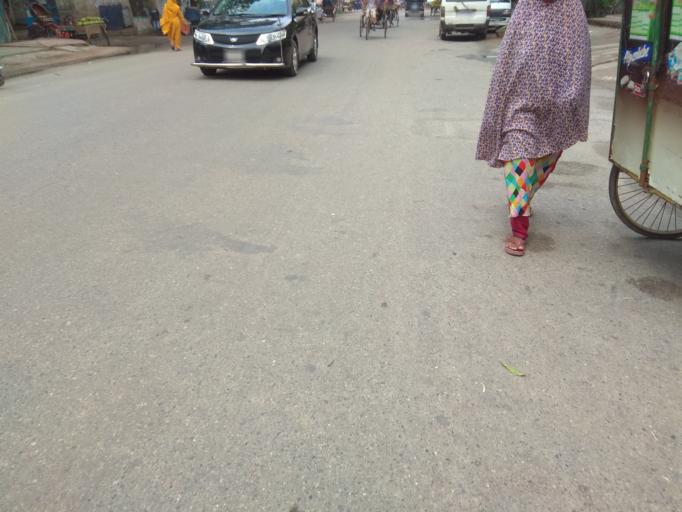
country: BD
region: Dhaka
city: Azimpur
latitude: 23.8044
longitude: 90.3560
